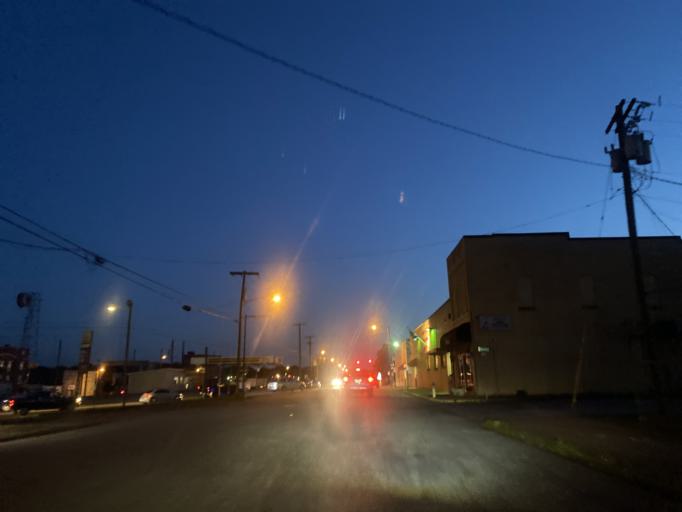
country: US
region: South Carolina
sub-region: Cherokee County
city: Gaffney
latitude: 35.0781
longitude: -81.6466
